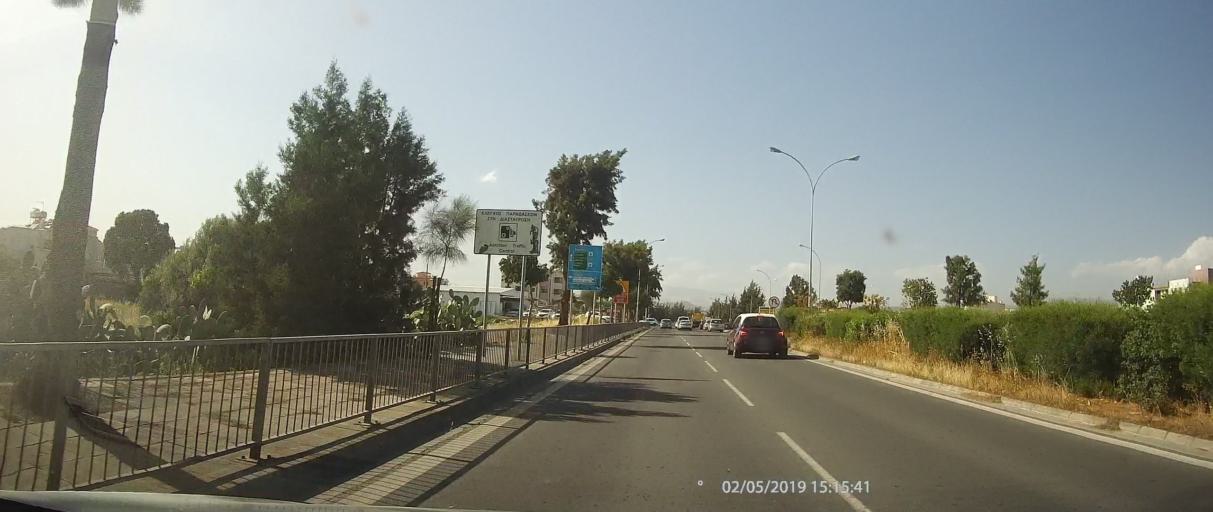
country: CY
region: Limassol
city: Limassol
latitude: 34.6788
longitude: 33.0102
